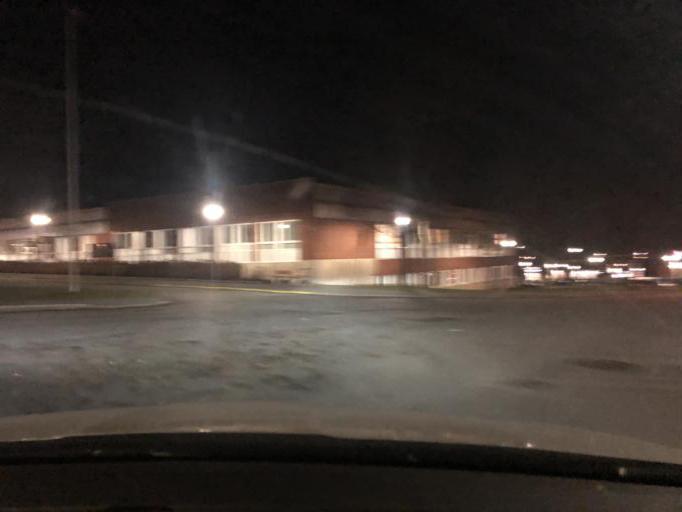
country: SE
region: Stockholm
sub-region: Haninge Kommun
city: Haninge
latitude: 59.1734
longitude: 18.1428
